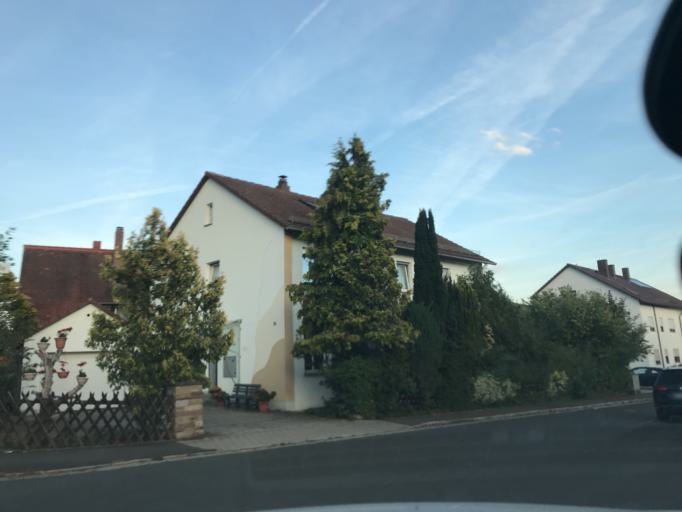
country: DE
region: Bavaria
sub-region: Upper Franconia
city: Pegnitz
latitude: 49.7447
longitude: 11.5377
